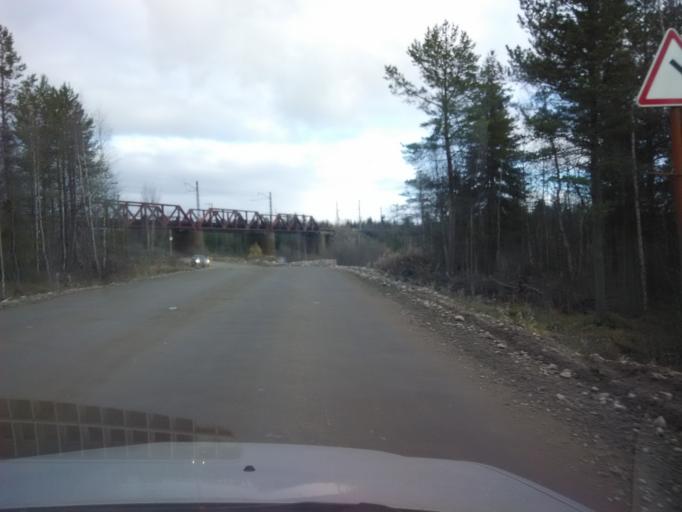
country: RU
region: Murmansk
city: Polyarnyye Zori
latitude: 67.3765
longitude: 32.5128
